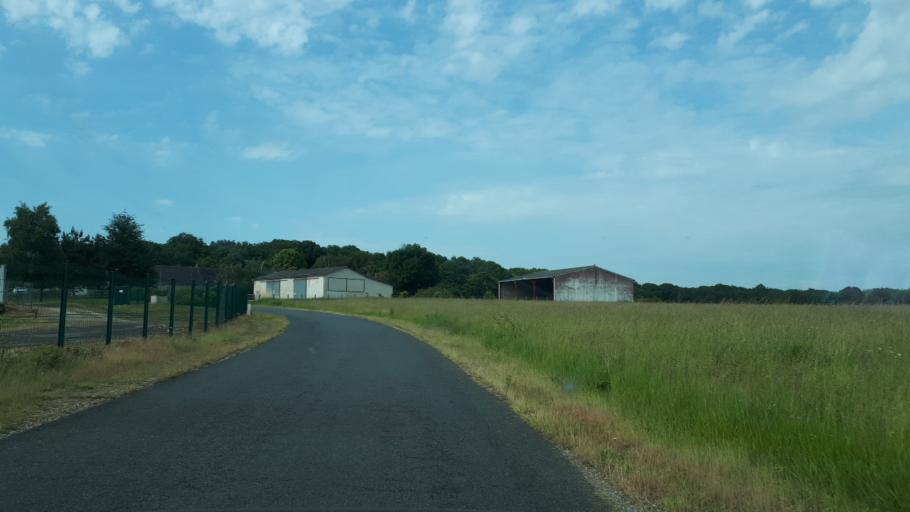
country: FR
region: Centre
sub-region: Departement d'Indre-et-Loire
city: Monnaie
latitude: 47.4949
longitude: 0.7756
